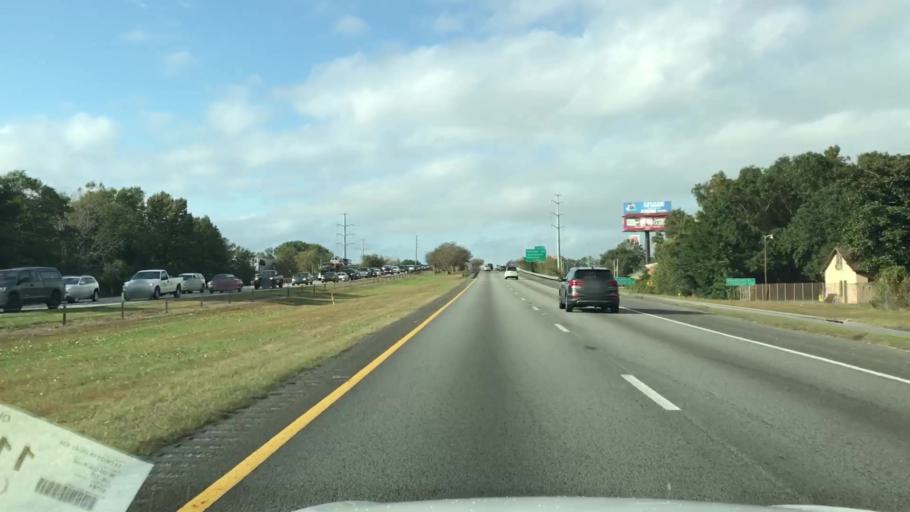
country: US
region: South Carolina
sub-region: Charleston County
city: North Charleston
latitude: 32.8506
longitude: -80.0191
